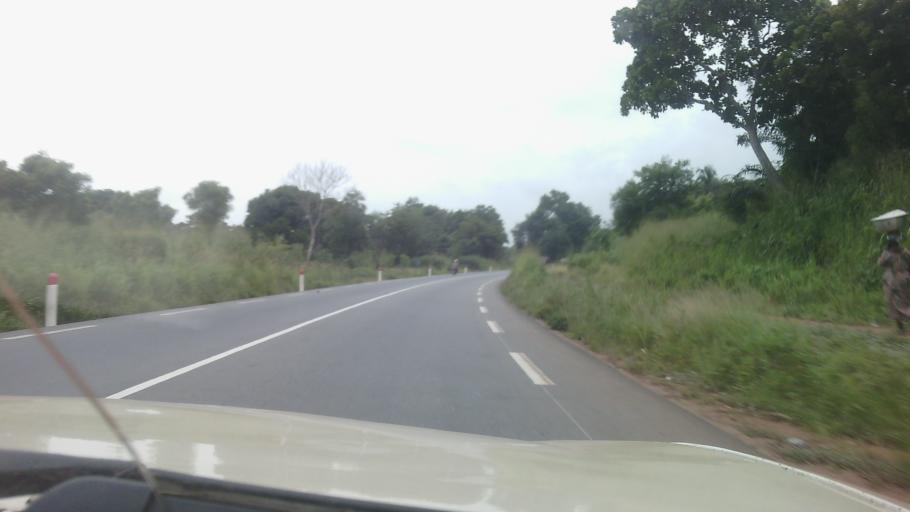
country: BJ
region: Mono
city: Come
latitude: 6.4043
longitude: 1.9642
